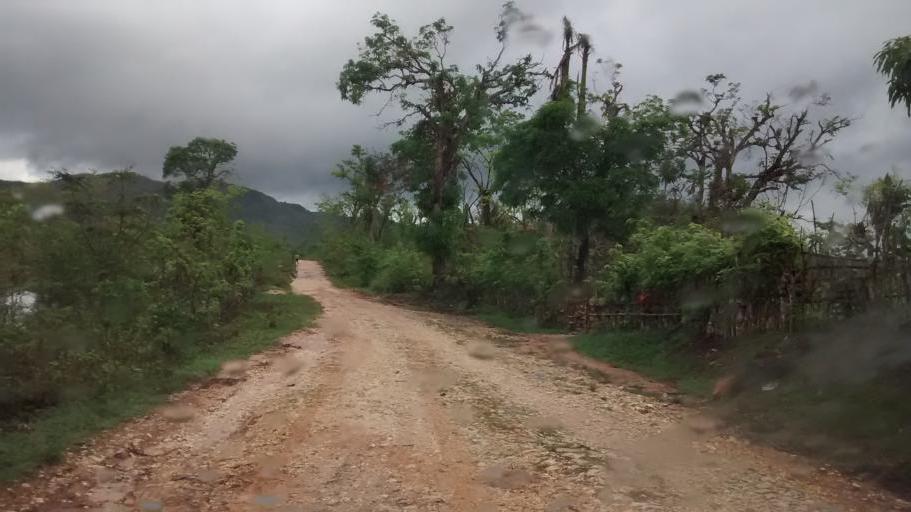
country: HT
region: Grandans
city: Corail
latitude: 18.5364
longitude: -73.9905
